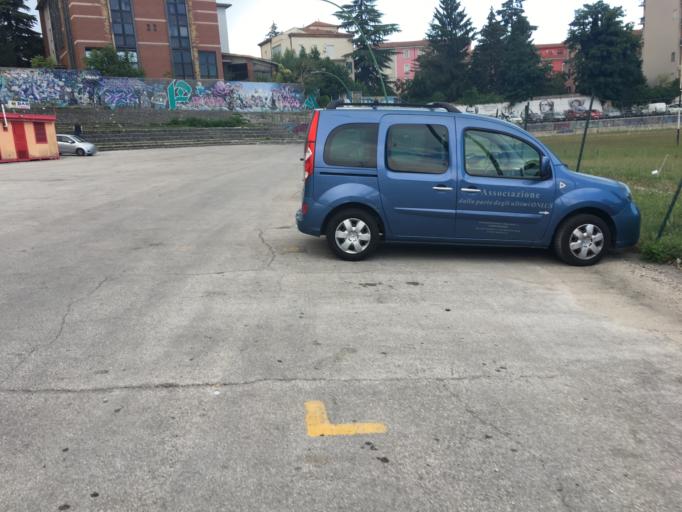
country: IT
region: Molise
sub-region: Provincia di Campobasso
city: Campobasso
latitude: 41.5545
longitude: 14.6599
